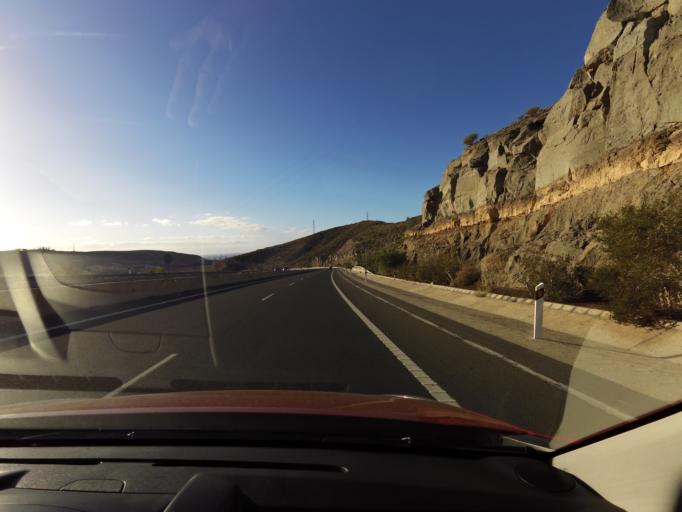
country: ES
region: Canary Islands
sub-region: Provincia de Las Palmas
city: Puerto Rico
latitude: 27.7713
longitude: -15.6743
